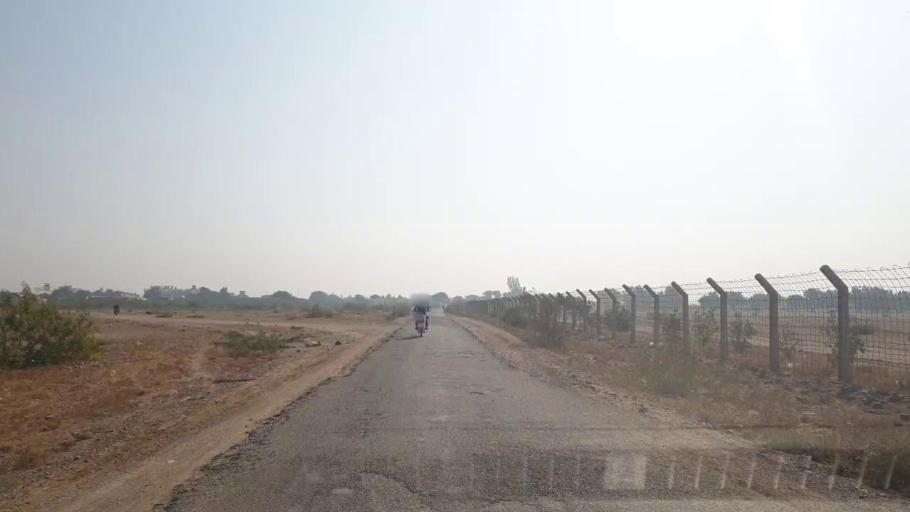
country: PK
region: Sindh
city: Jamshoro
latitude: 25.5358
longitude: 68.3374
